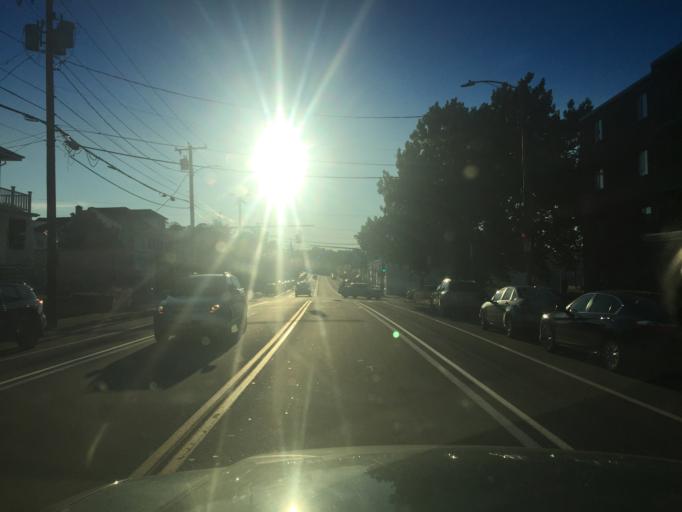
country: US
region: Massachusetts
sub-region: Norfolk County
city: Quincy
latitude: 42.2495
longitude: -70.9912
